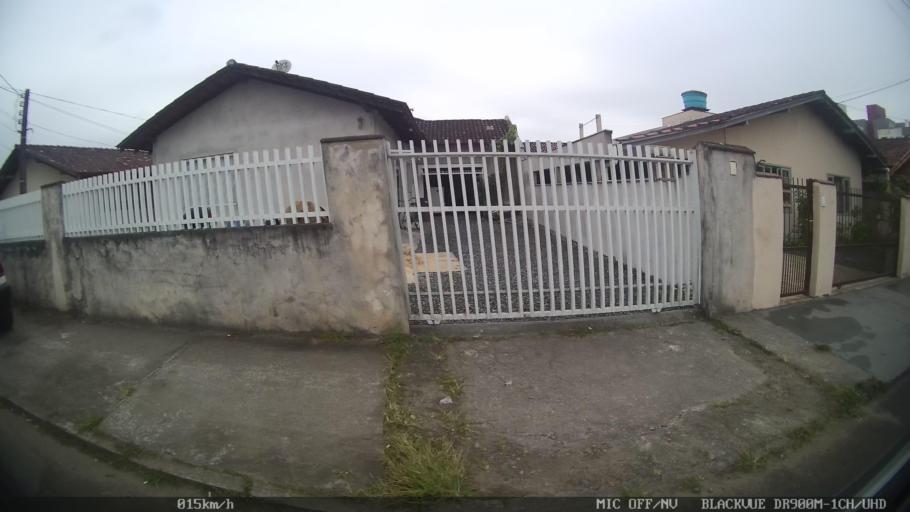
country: BR
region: Santa Catarina
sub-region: Joinville
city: Joinville
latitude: -26.2531
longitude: -48.8044
